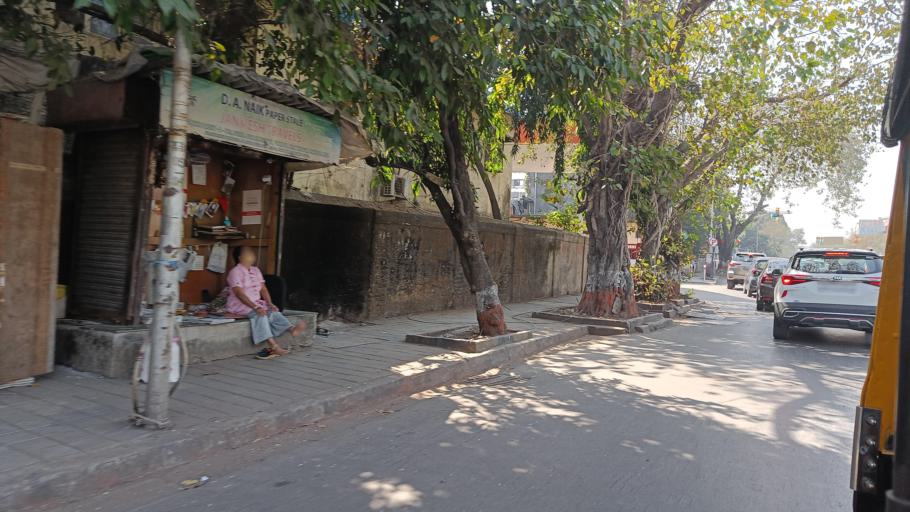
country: IN
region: Maharashtra
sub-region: Mumbai Suburban
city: Mumbai
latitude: 19.0905
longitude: 72.8384
